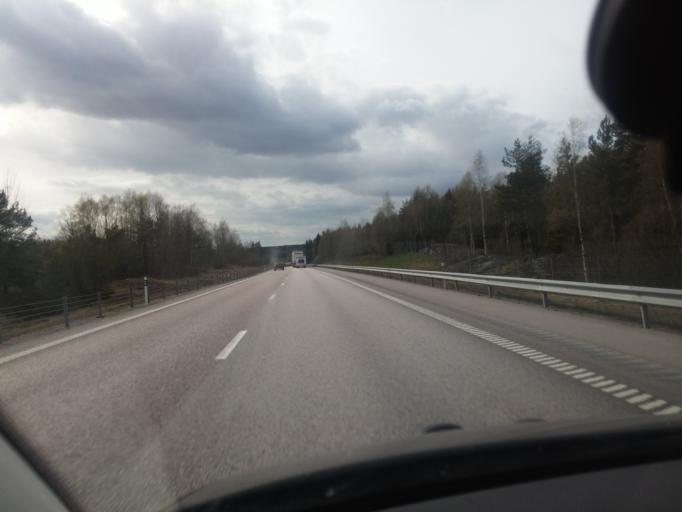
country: SE
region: Uppsala
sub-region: Enkopings Kommun
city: Grillby
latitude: 59.6323
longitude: 17.3160
